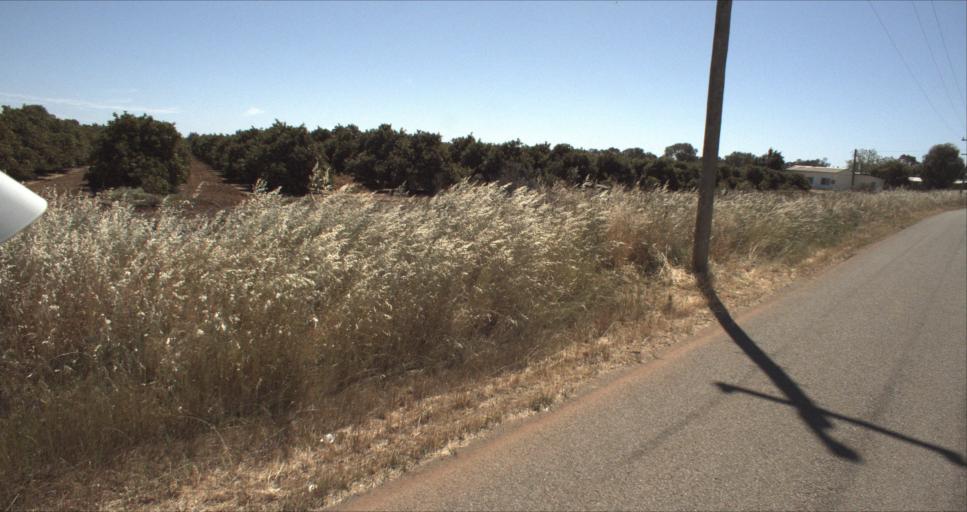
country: AU
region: New South Wales
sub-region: Leeton
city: Leeton
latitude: -34.5285
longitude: 146.3460
